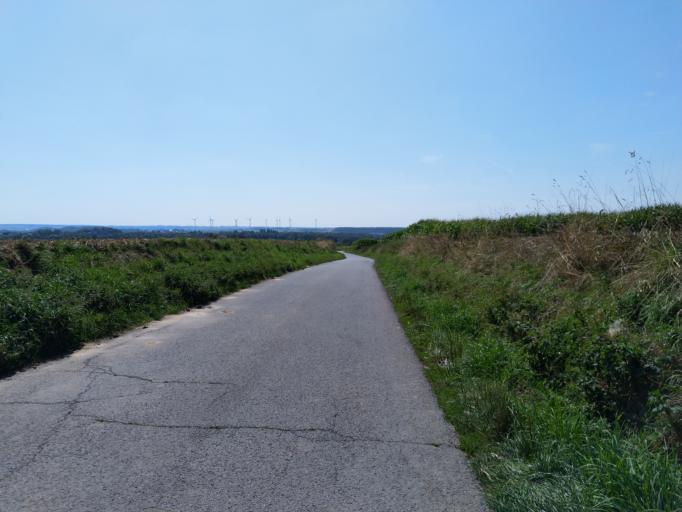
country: BE
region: Wallonia
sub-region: Province du Hainaut
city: Roeulx
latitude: 50.4831
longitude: 4.1022
